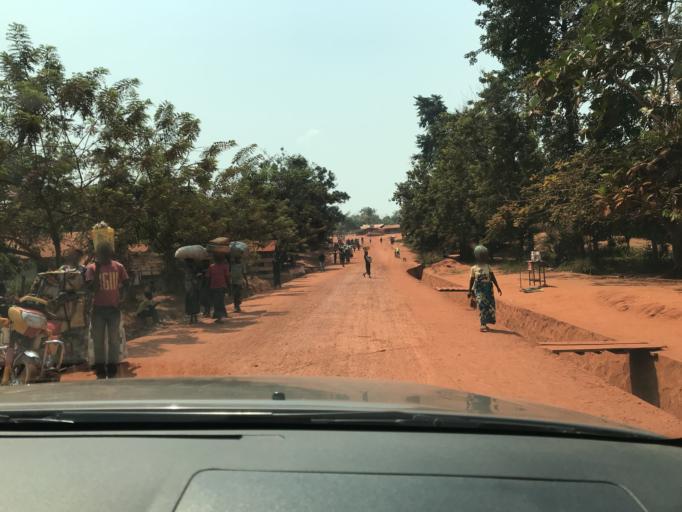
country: CD
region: Equateur
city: Gemena
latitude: 3.2248
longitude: 19.7757
